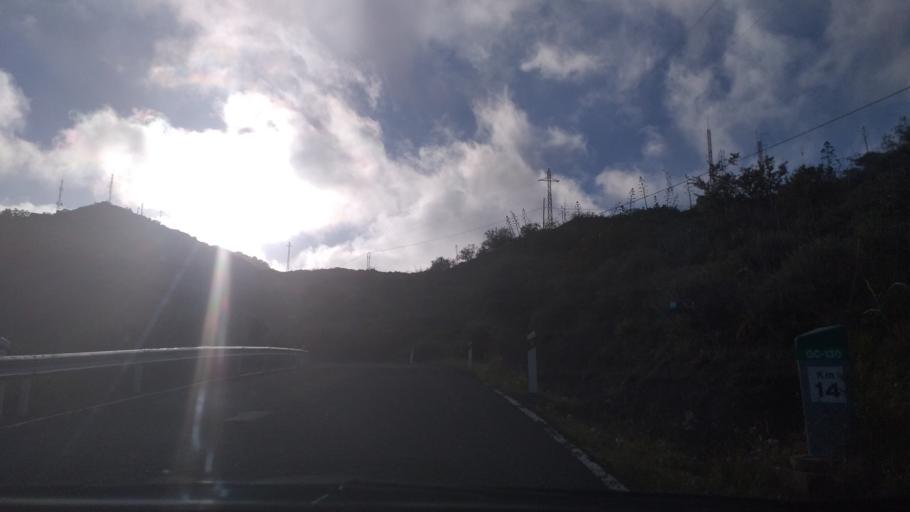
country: ES
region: Canary Islands
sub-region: Provincia de Las Palmas
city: Valsequillo de Gran Canaria
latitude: 27.9586
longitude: -15.5000
